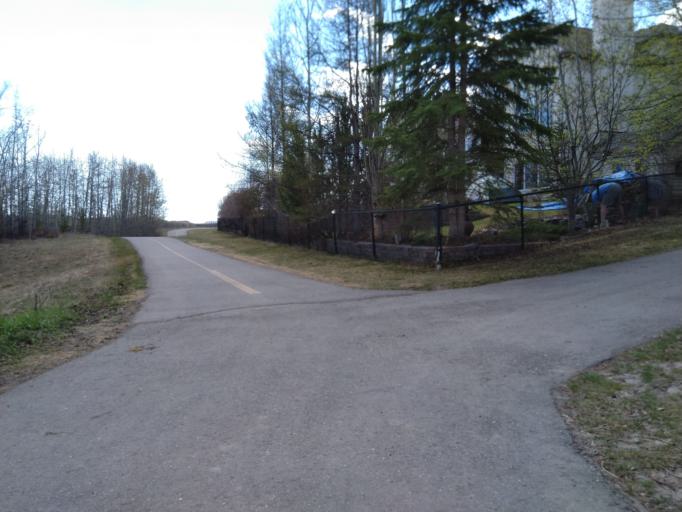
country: CA
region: Alberta
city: Calgary
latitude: 51.1210
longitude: -114.2375
